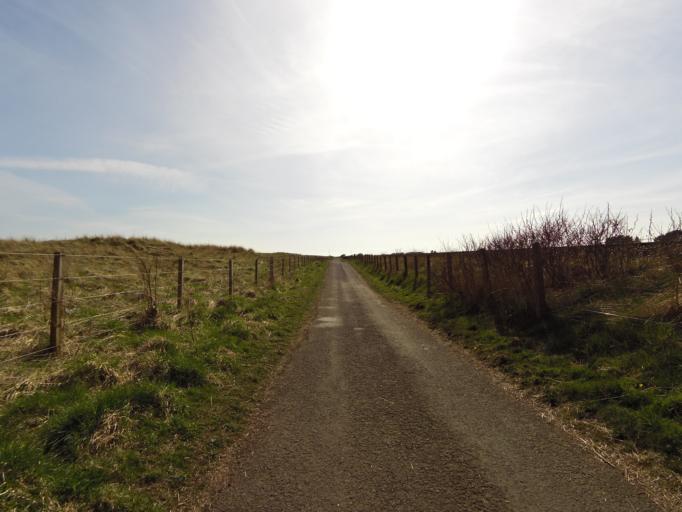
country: GB
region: Scotland
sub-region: Angus
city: Arbroath
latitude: 56.5380
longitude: -2.6269
